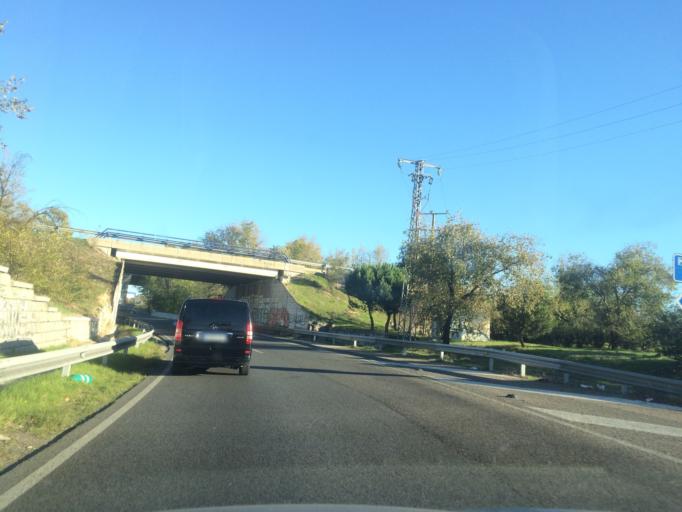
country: ES
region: Madrid
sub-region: Provincia de Madrid
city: San Blas
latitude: 40.4491
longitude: -3.5908
